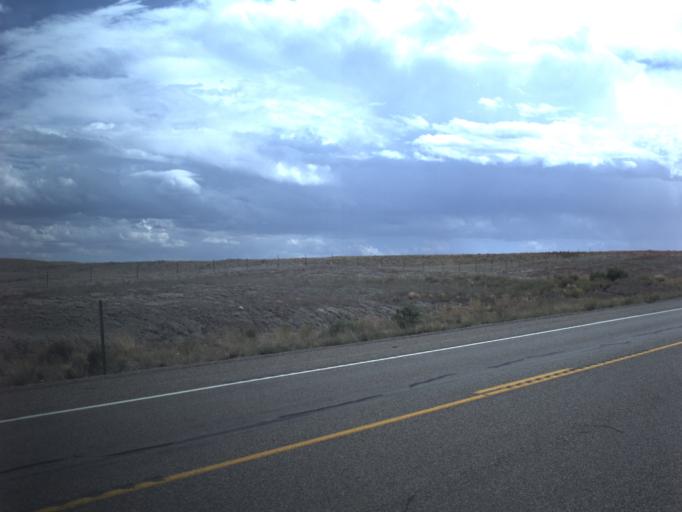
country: US
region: Utah
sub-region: Carbon County
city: Price
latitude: 39.5055
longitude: -110.8370
